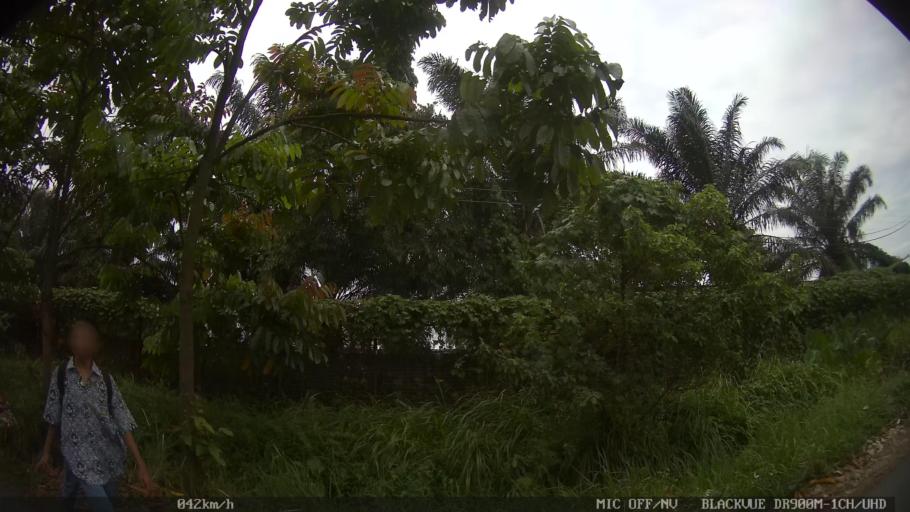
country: ID
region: North Sumatra
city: Sunggal
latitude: 3.6179
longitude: 98.5805
